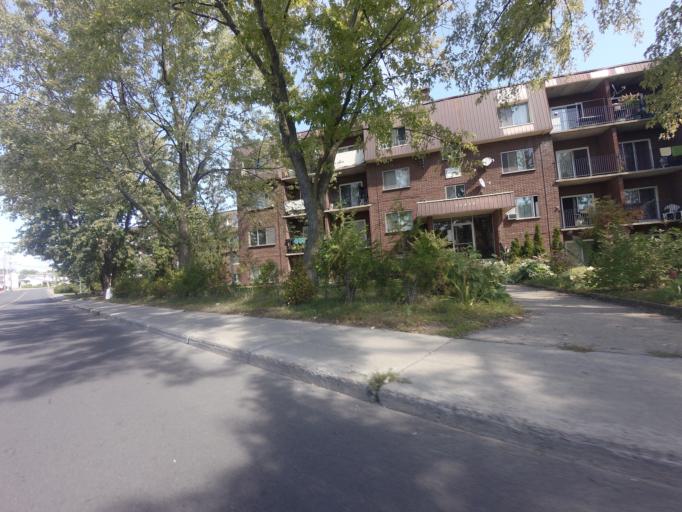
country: CA
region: Quebec
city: Kirkland
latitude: 45.4755
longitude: -73.8744
